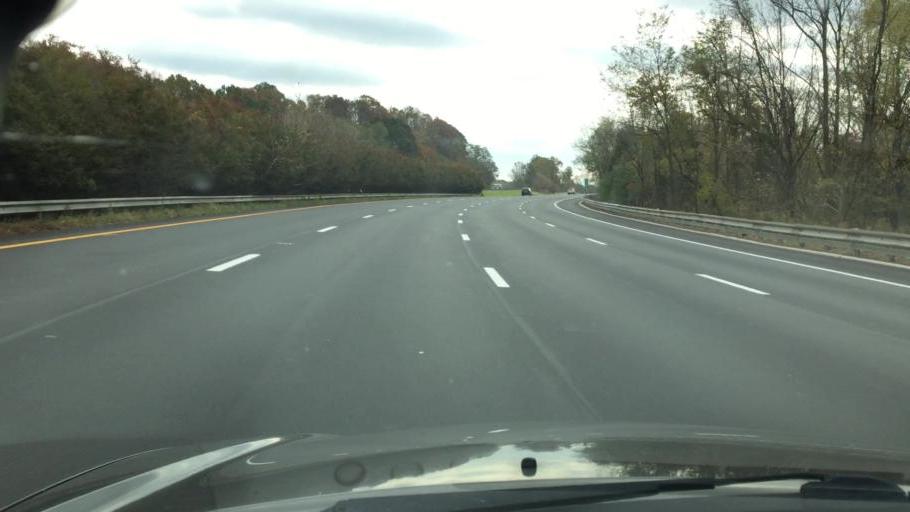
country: US
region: New Jersey
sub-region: Warren County
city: Belvidere
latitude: 40.9281
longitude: -75.0704
